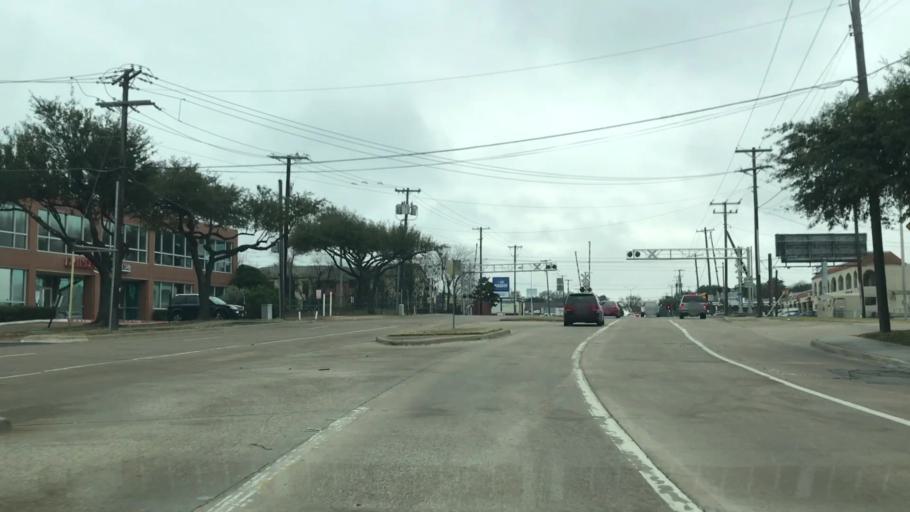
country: US
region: Texas
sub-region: Dallas County
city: Richardson
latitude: 32.8970
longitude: -96.7179
